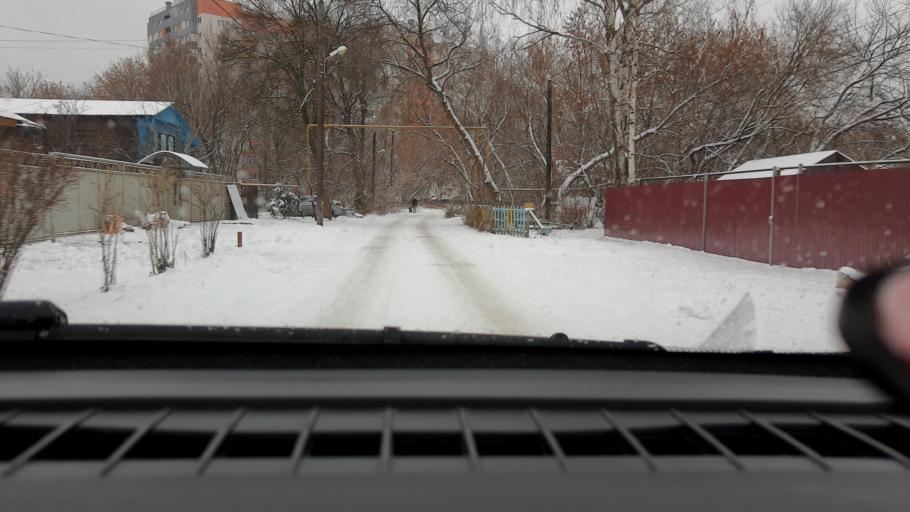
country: RU
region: Nizjnij Novgorod
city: Nizhniy Novgorod
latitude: 56.3337
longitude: 43.9119
